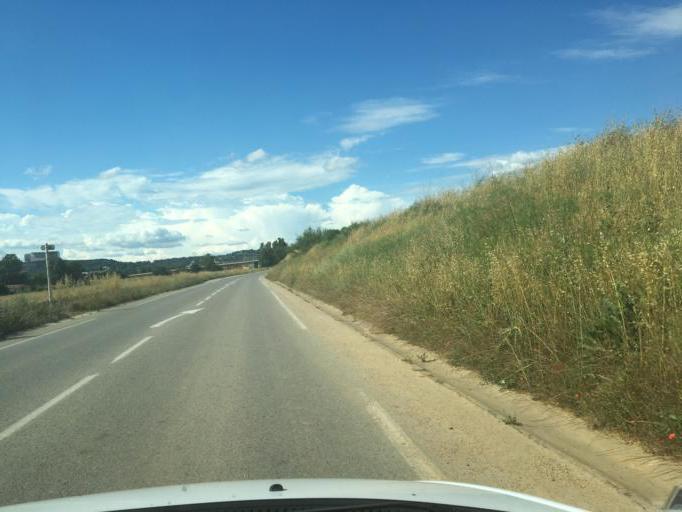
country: FR
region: Provence-Alpes-Cote d'Azur
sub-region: Departement des Bouches-du-Rhone
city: Eguilles
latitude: 43.5412
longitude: 5.3482
